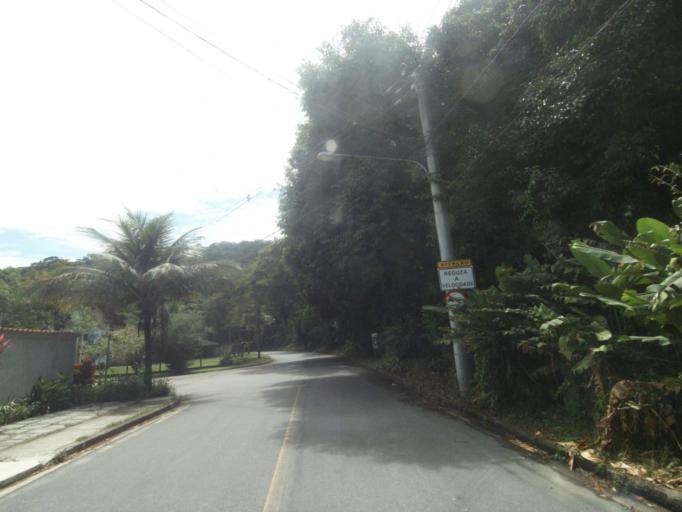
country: BR
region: Rio de Janeiro
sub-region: Niteroi
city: Niteroi
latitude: -22.9531
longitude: -43.0220
